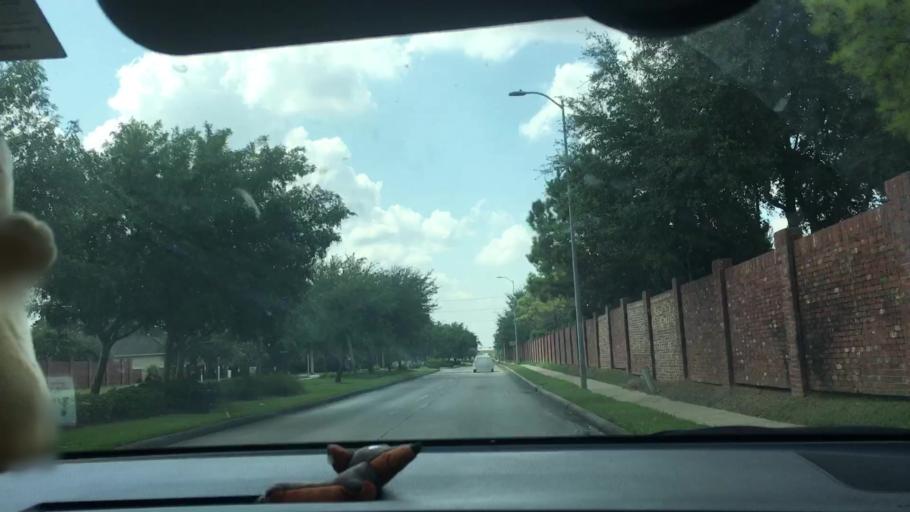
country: US
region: Texas
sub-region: Harris County
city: Bunker Hill Village
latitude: 29.7233
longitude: -95.5717
